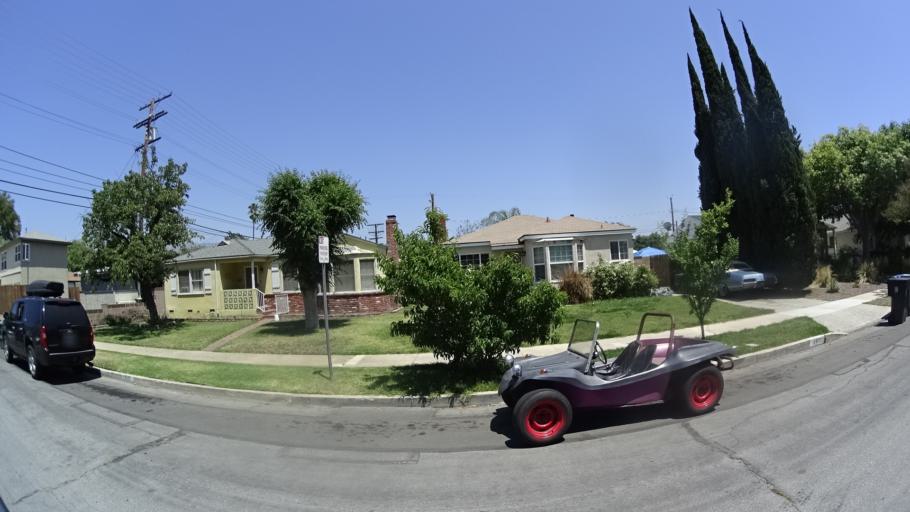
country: US
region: California
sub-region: Los Angeles County
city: North Hollywood
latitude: 34.1841
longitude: -118.3458
